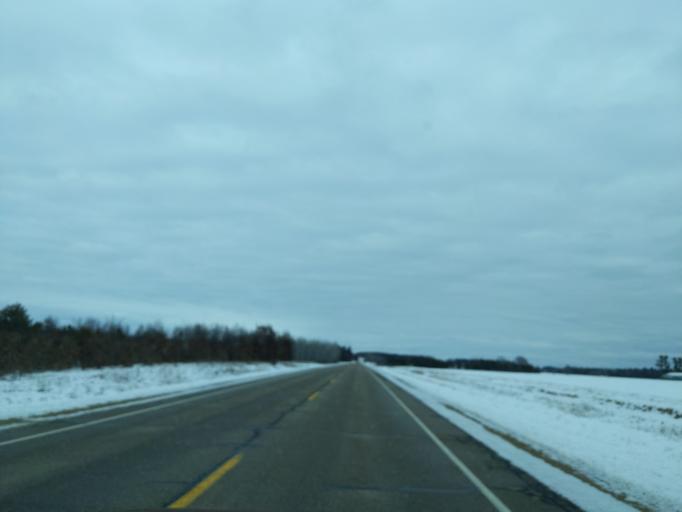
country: US
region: Wisconsin
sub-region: Waushara County
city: Wautoma
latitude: 43.9883
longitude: -89.3276
